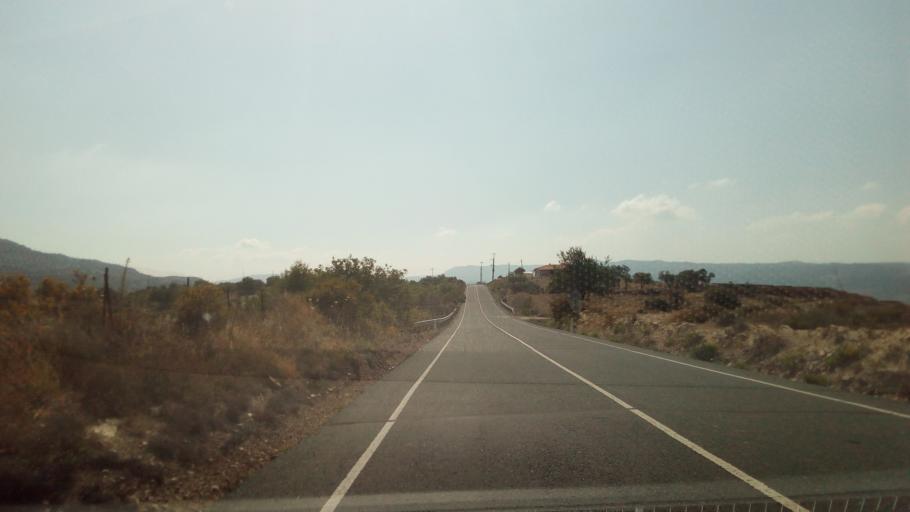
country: CY
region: Limassol
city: Pissouri
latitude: 34.7914
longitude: 32.6341
